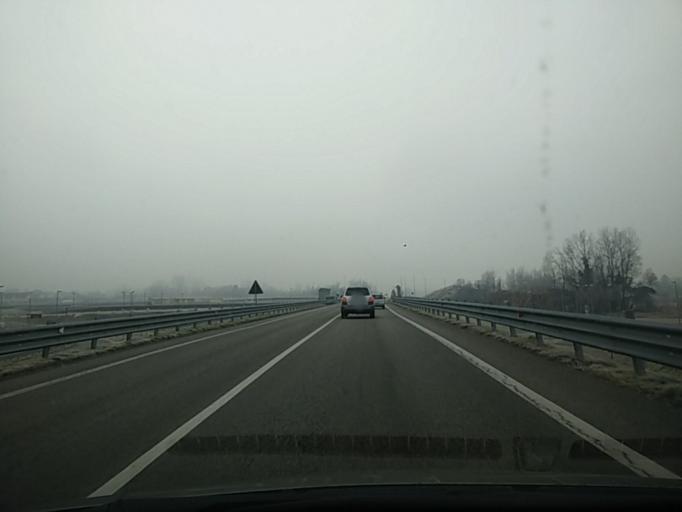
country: IT
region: Veneto
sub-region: Provincia di Belluno
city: Seren del Grappa
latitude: 46.0066
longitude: 11.8702
